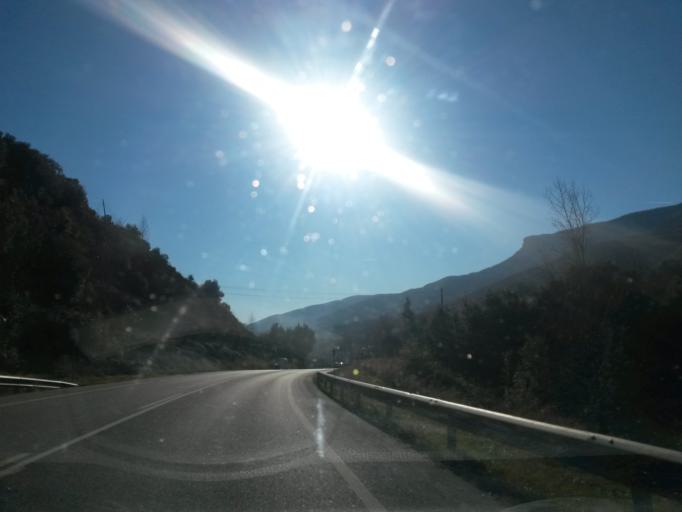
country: ES
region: Catalonia
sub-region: Provincia de Girona
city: les Planes d'Hostoles
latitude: 42.0651
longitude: 2.5308
